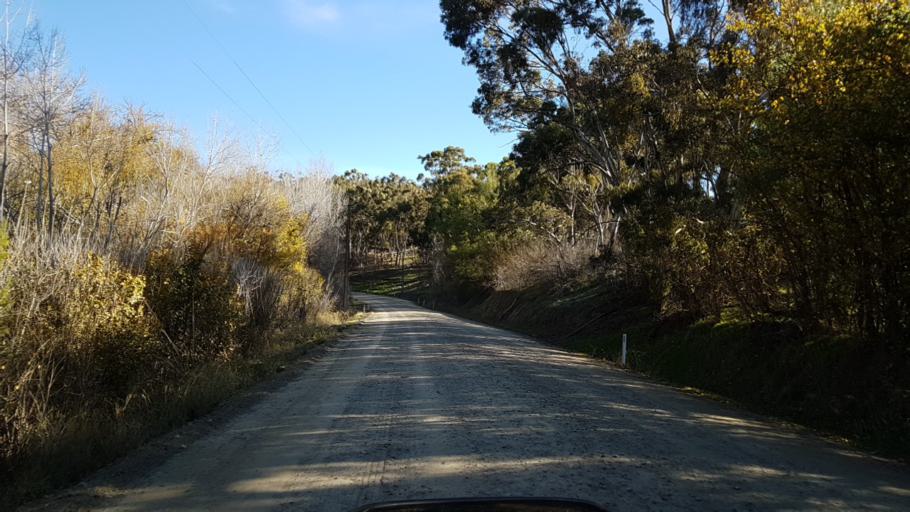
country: AU
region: South Australia
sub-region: Northern Areas
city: Jamestown
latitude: -33.2779
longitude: 138.5688
